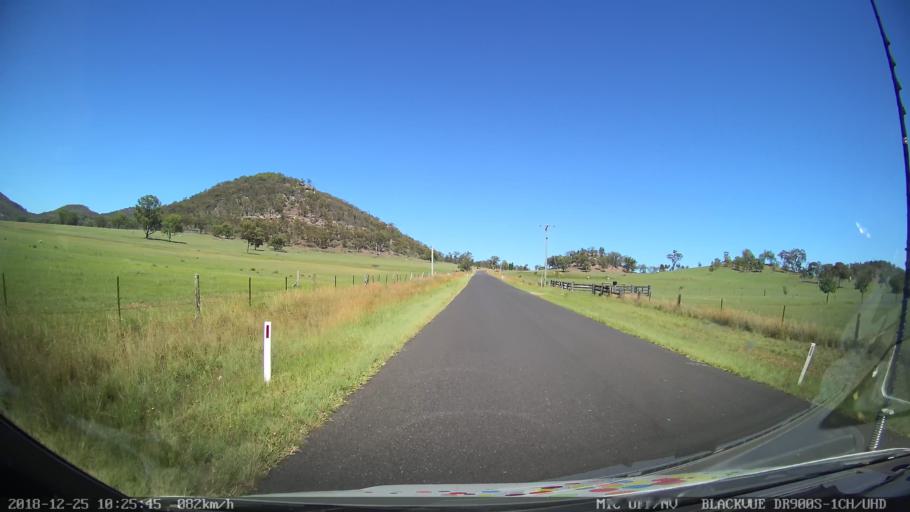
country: AU
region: New South Wales
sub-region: Muswellbrook
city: Denman
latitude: -32.3913
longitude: 150.4946
